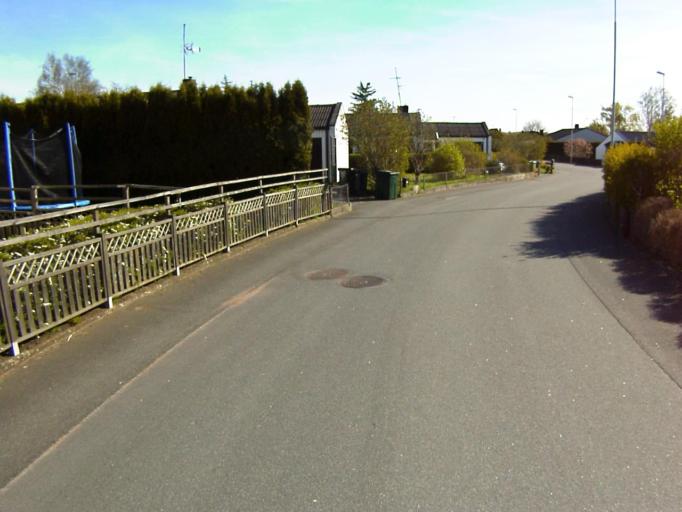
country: SE
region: Skane
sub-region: Kristianstads Kommun
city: Kristianstad
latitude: 56.0104
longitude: 14.1518
